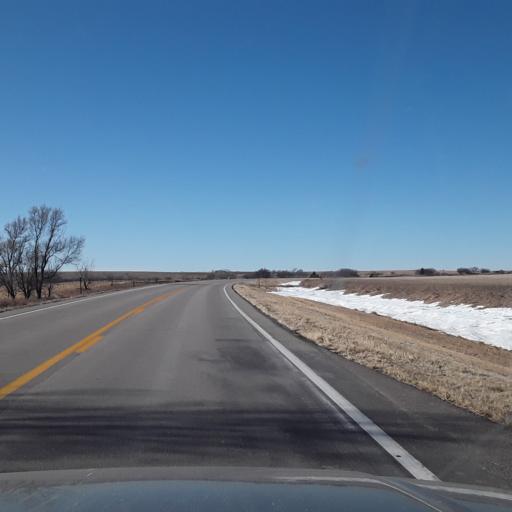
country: US
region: Nebraska
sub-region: Dawson County
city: Cozad
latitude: 40.6710
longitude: -100.0992
